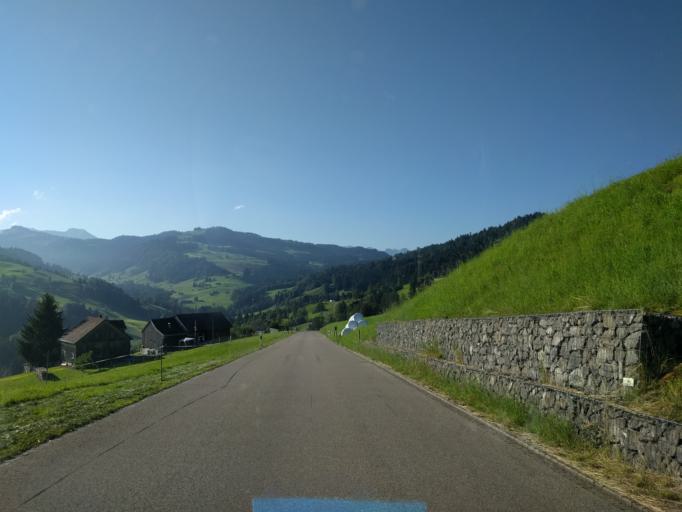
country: CH
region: Saint Gallen
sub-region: Wahlkreis Toggenburg
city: Sankt Peterzell
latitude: 47.2981
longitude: 9.1778
